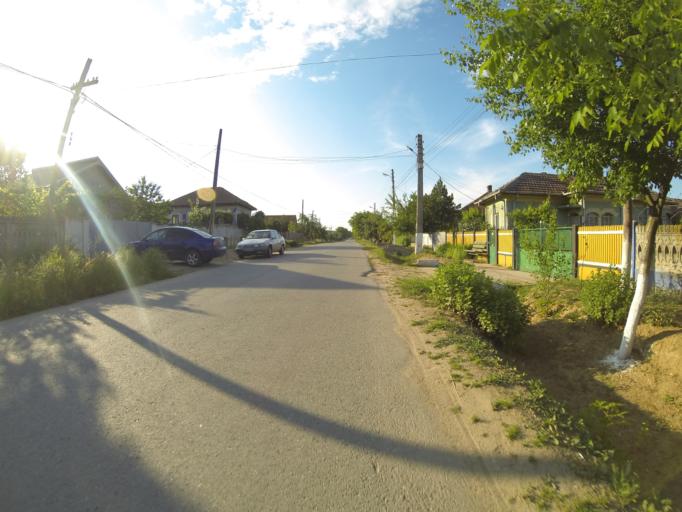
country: RO
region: Dolj
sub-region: Comuna Tuglui
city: Tuglui
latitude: 44.2110
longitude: 23.7938
